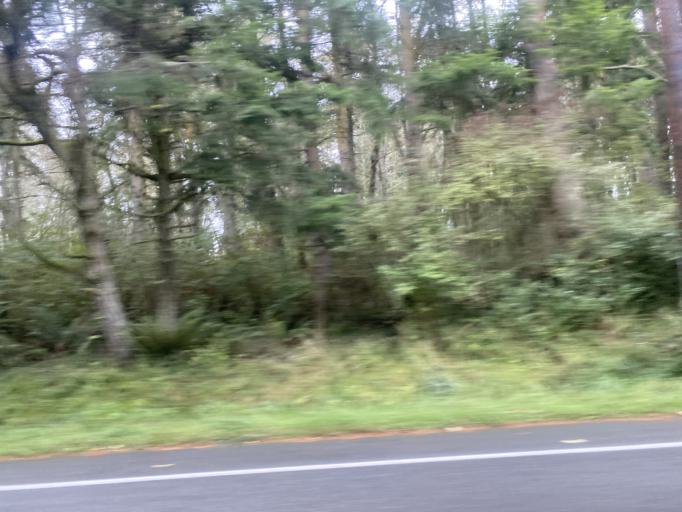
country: US
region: Washington
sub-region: Island County
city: Freeland
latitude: 48.0545
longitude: -122.5067
